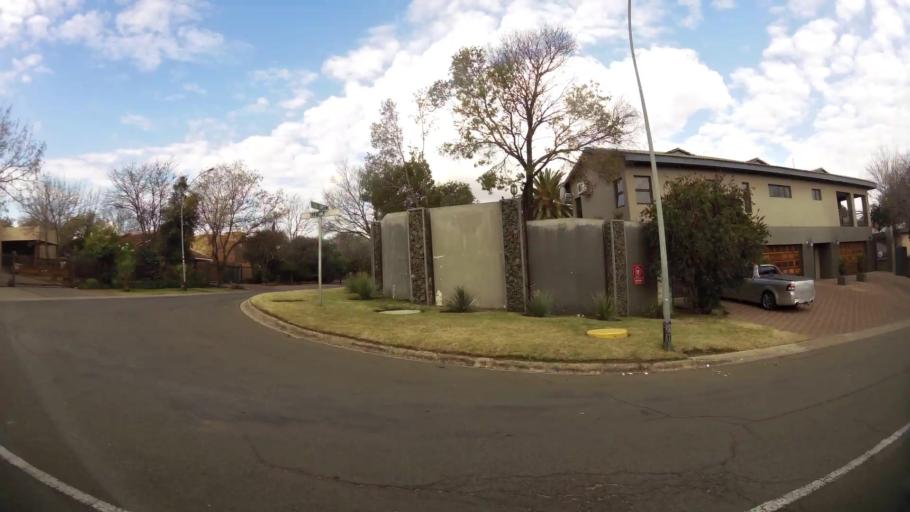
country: ZA
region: Orange Free State
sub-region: Mangaung Metropolitan Municipality
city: Bloemfontein
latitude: -29.0855
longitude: 26.1990
